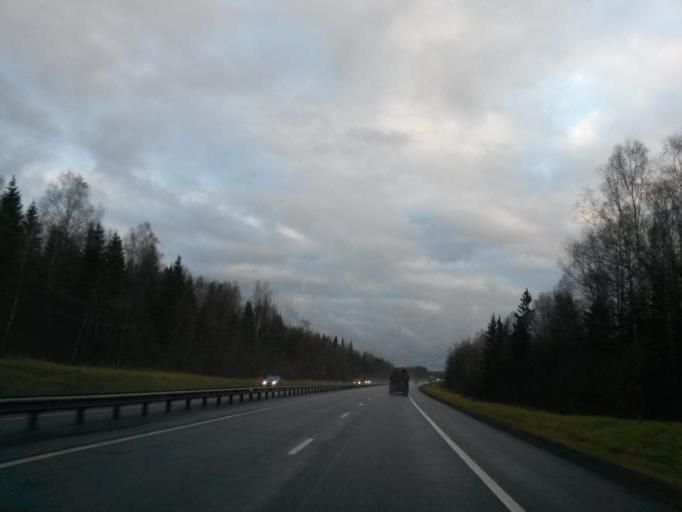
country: RU
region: Moskovskaya
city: Svatkovo
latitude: 56.4119
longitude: 38.3289
